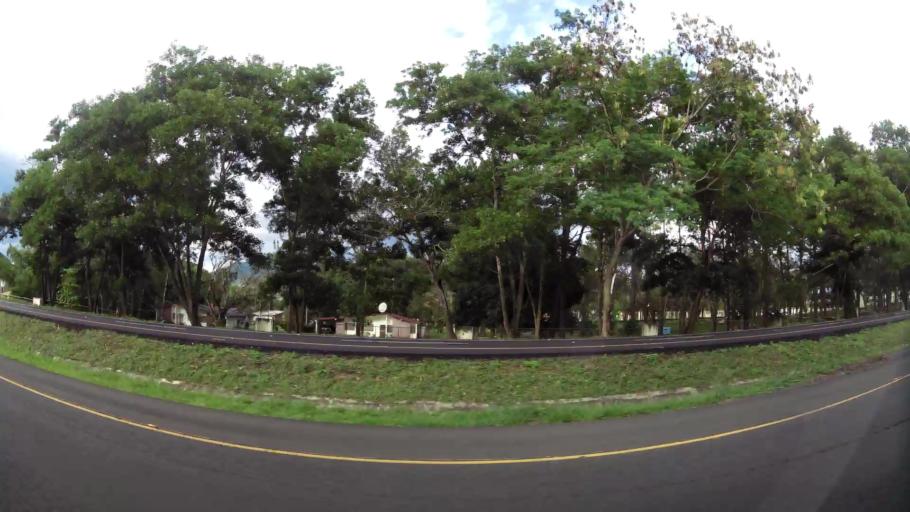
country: DO
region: Monsenor Nouel
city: Piedra Blanca
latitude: 18.8676
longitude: -70.3580
